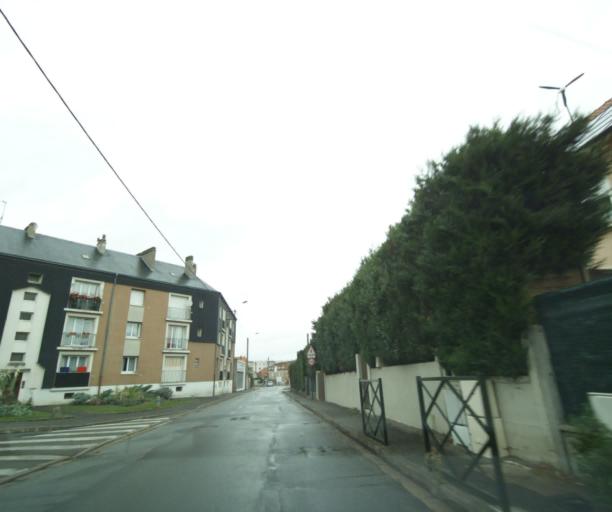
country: FR
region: Centre
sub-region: Departement d'Eure-et-Loir
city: Vernouillet
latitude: 48.7263
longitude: 1.3784
